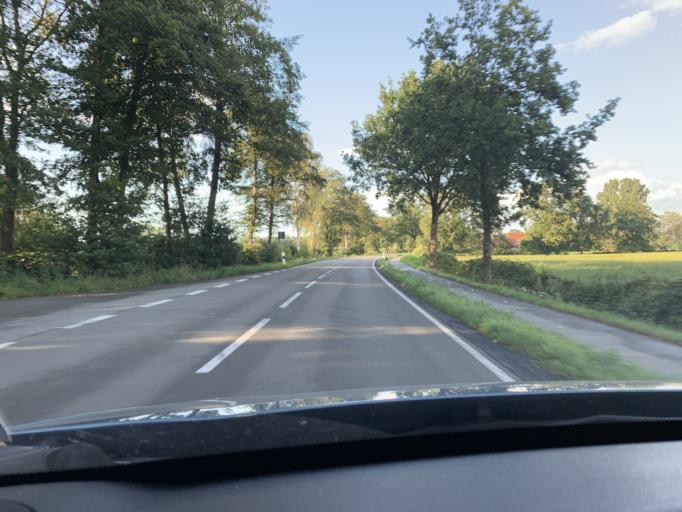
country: DE
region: Lower Saxony
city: Edewecht
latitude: 53.1039
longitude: 7.9514
